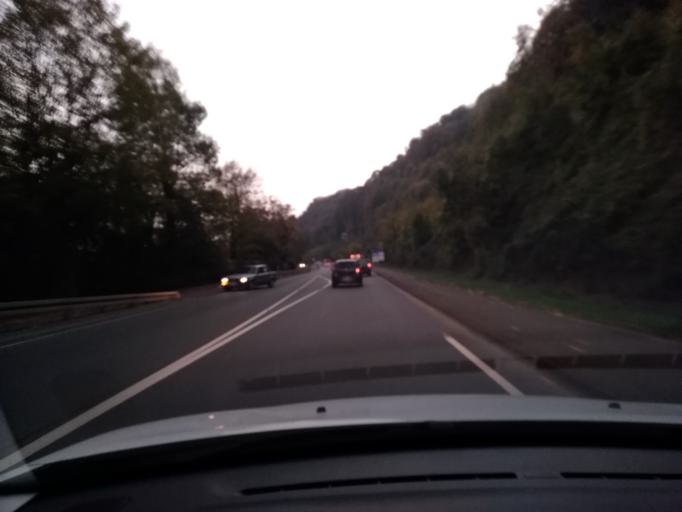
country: FR
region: Lorraine
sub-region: Departement de la Moselle
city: Alsting
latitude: 49.2048
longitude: 7.0175
